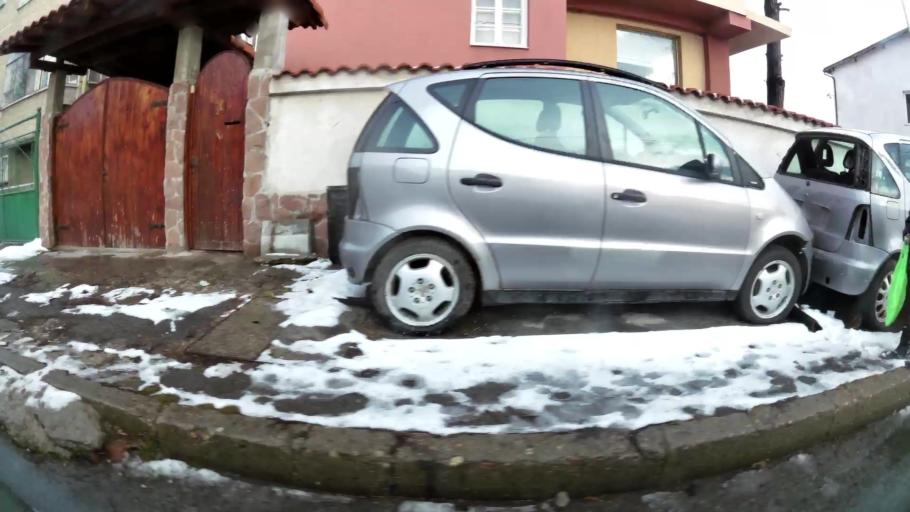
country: BG
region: Sofia-Capital
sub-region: Stolichna Obshtina
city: Sofia
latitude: 42.7129
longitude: 23.3476
